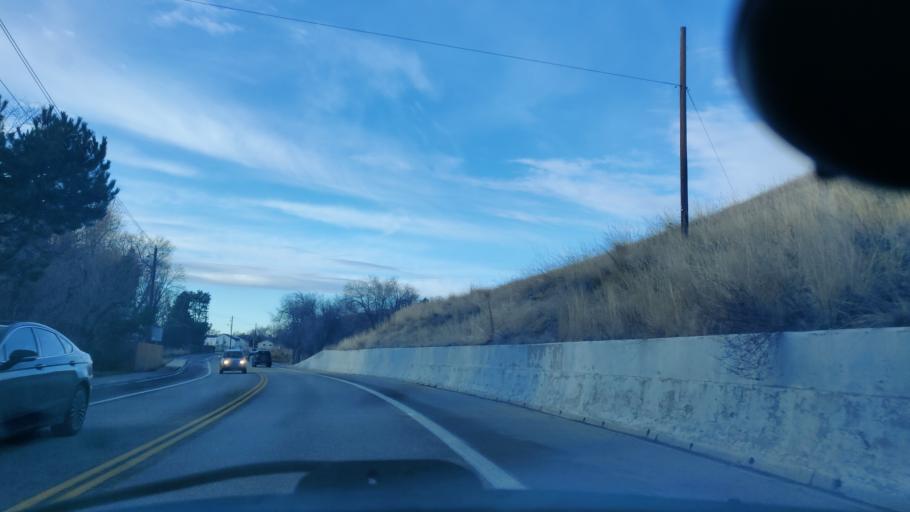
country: US
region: Idaho
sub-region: Ada County
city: Garden City
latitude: 43.6511
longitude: -116.2263
